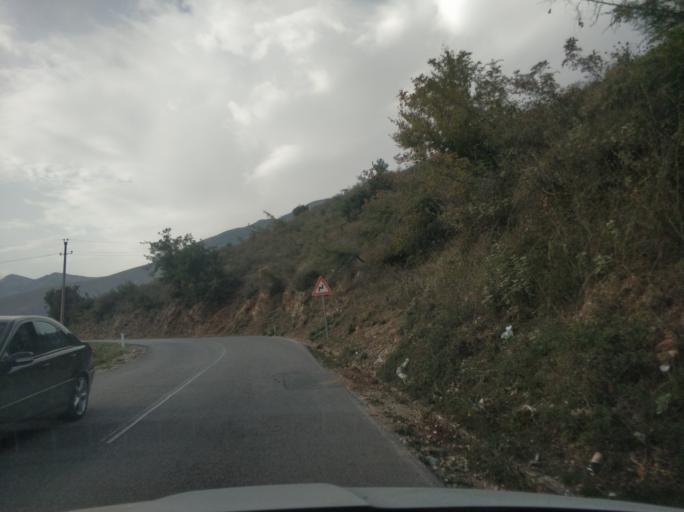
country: AL
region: Vlore
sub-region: Rrethi i Sarandes
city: Dhiver
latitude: 39.9228
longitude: 20.2034
